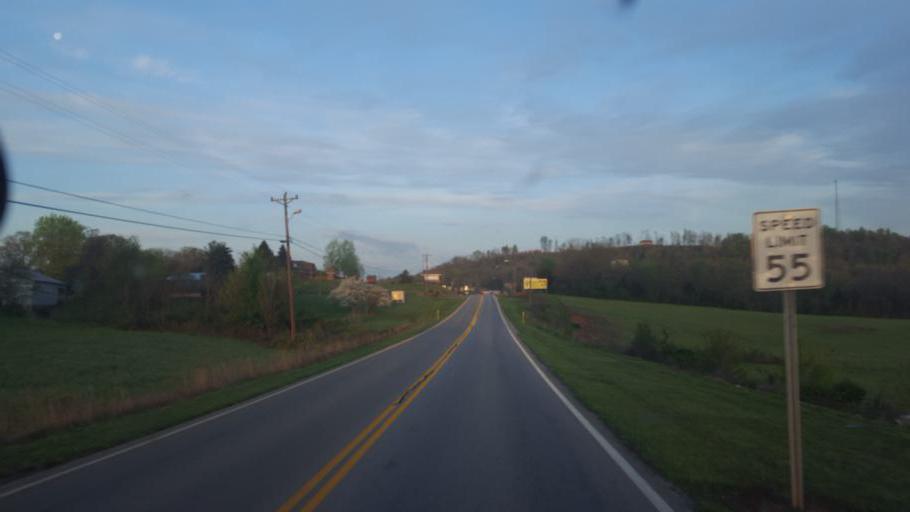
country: US
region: Kentucky
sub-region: Barren County
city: Cave City
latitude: 37.1355
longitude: -85.9880
